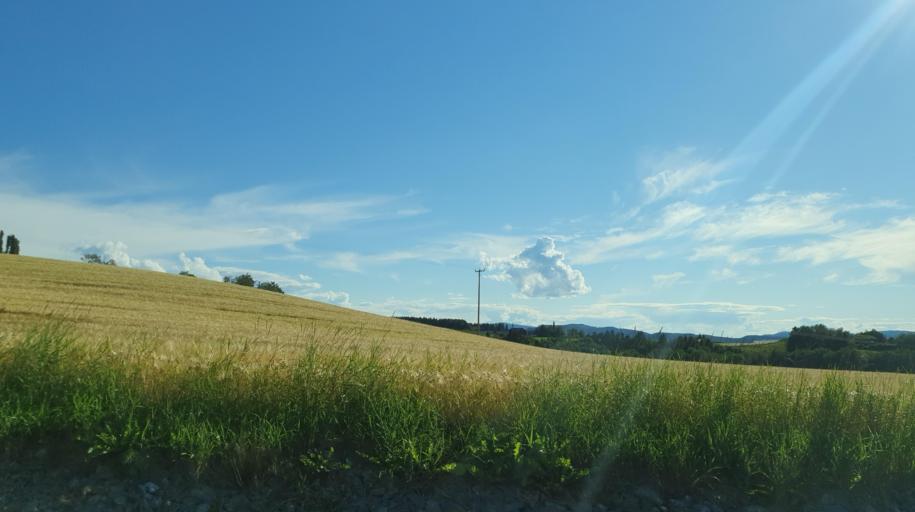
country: NO
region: Nord-Trondelag
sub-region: Levanger
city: Skogn
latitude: 63.7001
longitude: 11.2454
